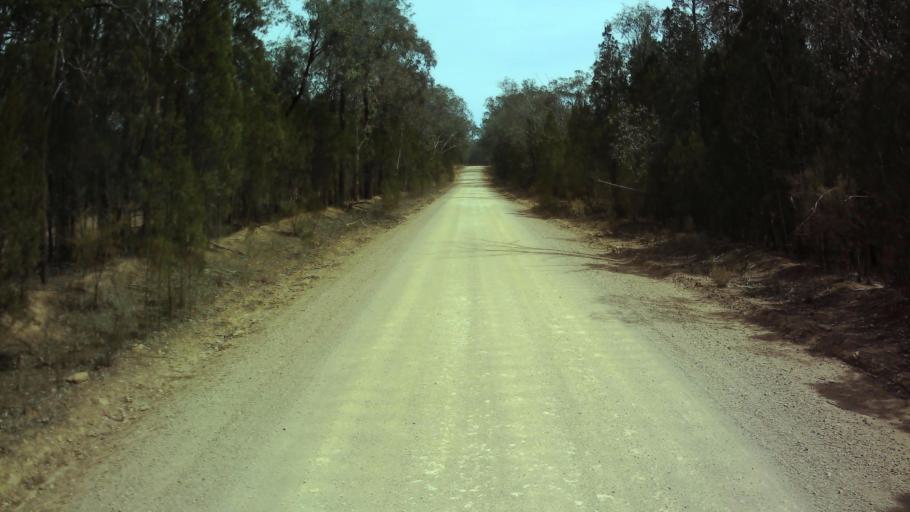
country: AU
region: New South Wales
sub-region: Weddin
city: Grenfell
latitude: -33.9085
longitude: 148.4104
